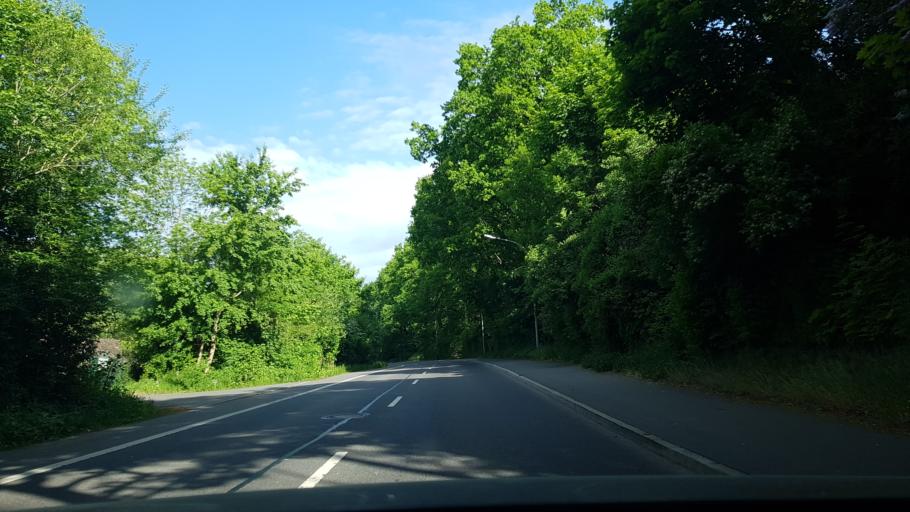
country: DE
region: Saxony
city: Wittgensdorf
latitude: 50.8773
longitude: 12.9047
